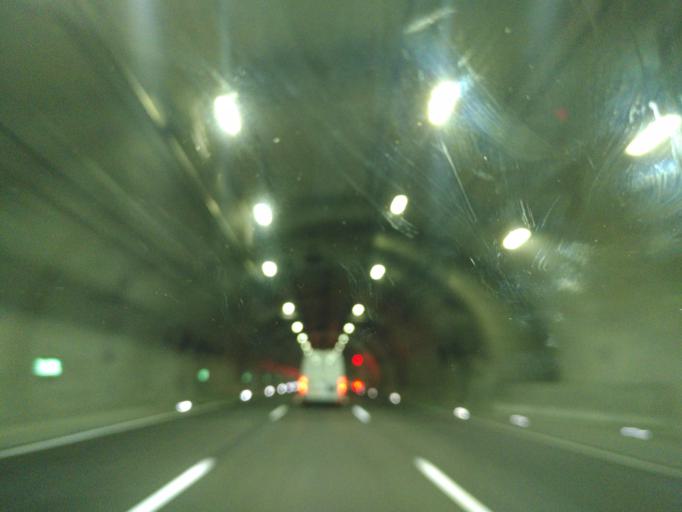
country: DE
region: Thuringia
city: Bucha
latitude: 50.8761
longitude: 11.5557
